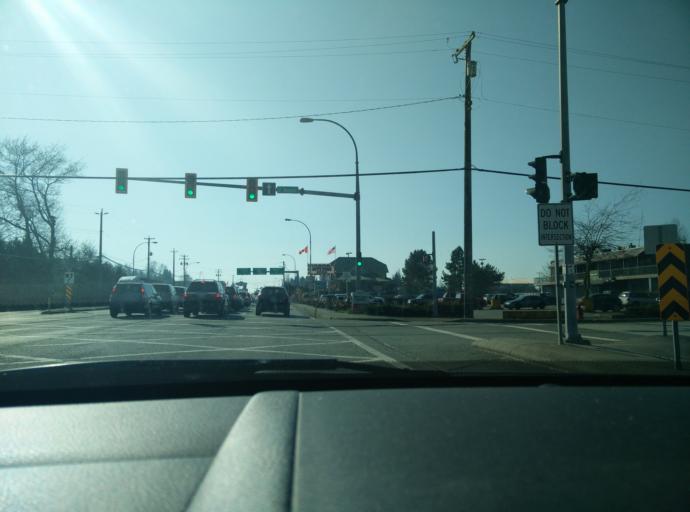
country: US
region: Washington
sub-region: Whatcom County
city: Blaine
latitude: 49.0057
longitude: -122.7355
